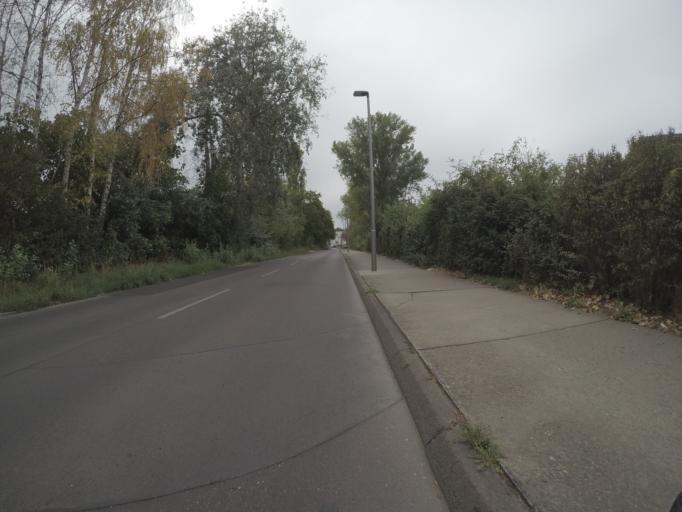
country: DE
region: Berlin
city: Neu-Hohenschoenhausen
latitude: 52.5600
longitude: 13.5166
